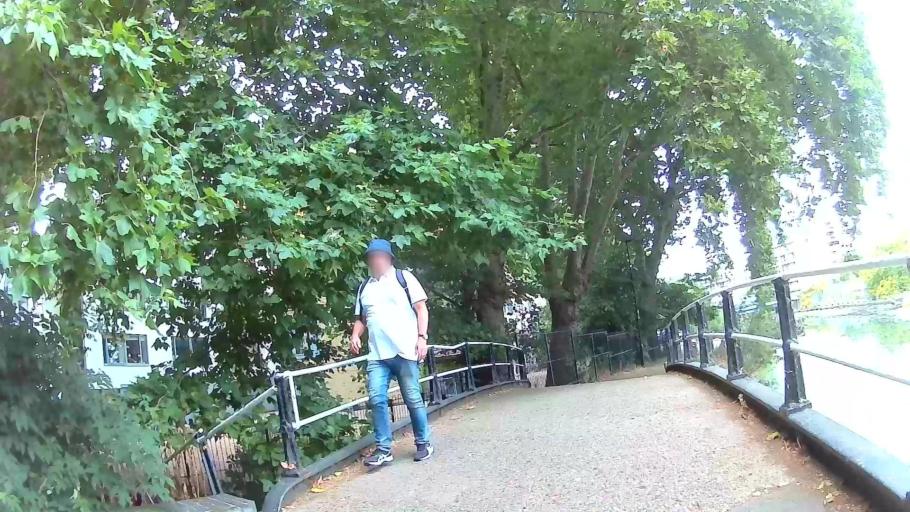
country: GB
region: England
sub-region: Greater London
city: Hackney
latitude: 51.5611
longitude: -0.0447
